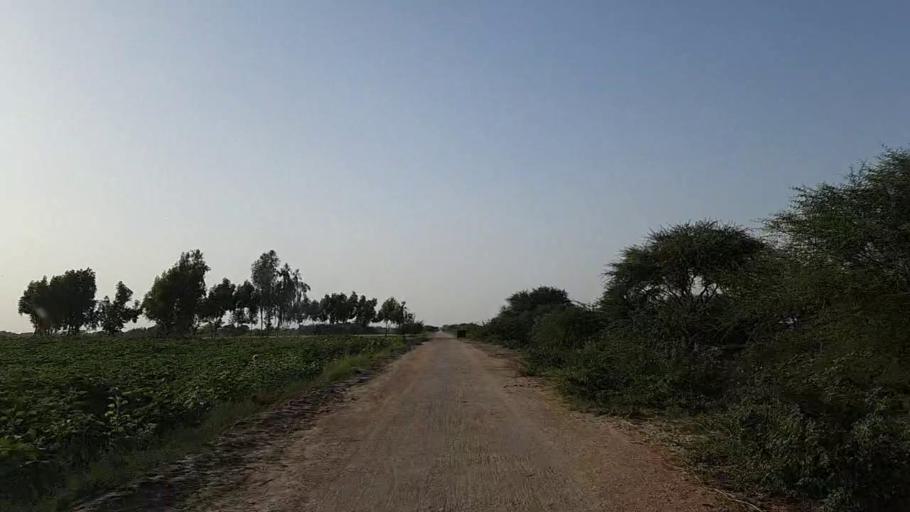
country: PK
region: Sindh
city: Jati
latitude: 24.3295
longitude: 68.1599
